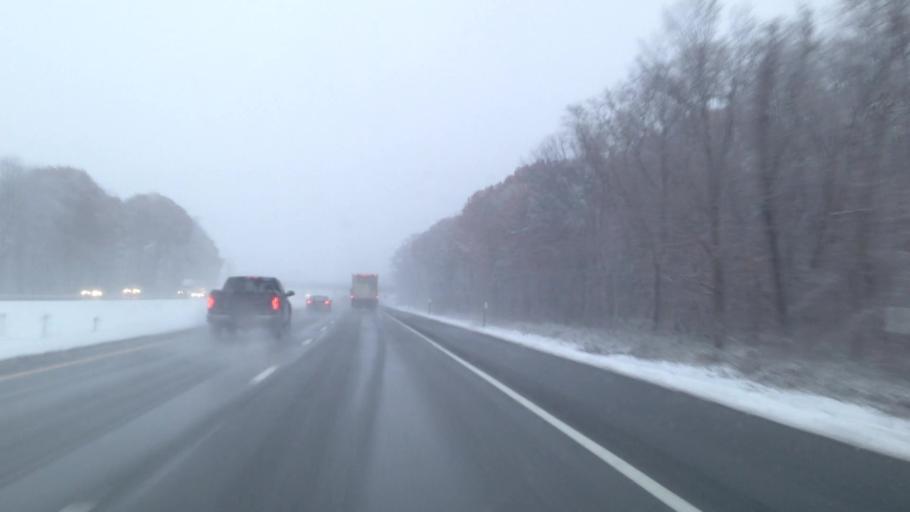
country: US
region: New York
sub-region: Onondaga County
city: Minoa
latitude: 43.0921
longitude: -75.9577
